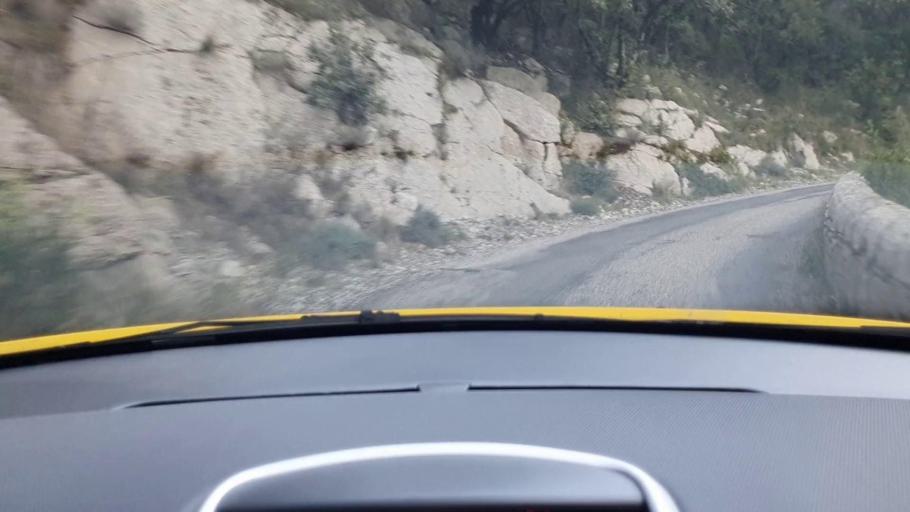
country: FR
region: Languedoc-Roussillon
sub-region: Departement du Gard
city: Saint-Hippolyte-du-Fort
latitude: 43.9638
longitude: 3.8091
